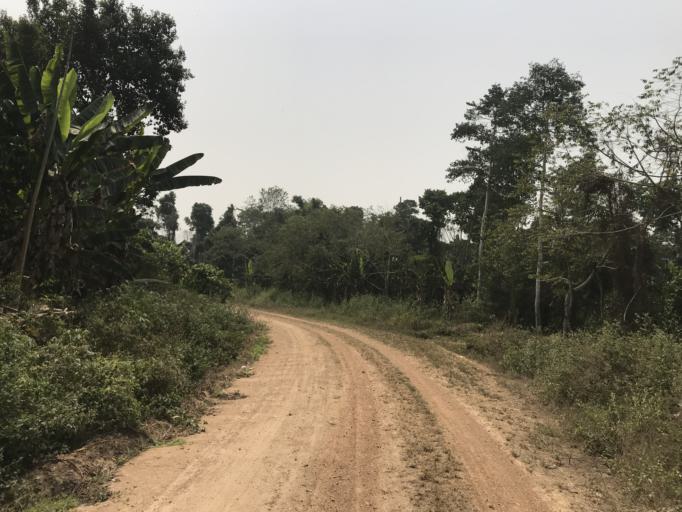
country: NG
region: Osun
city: Ifetedo
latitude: 7.0371
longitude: 4.4751
